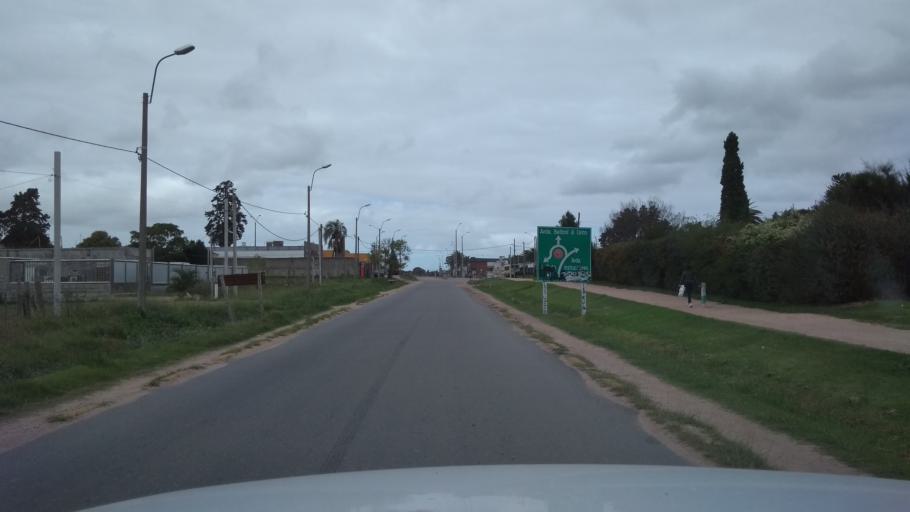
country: UY
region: Canelones
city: Toledo
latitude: -34.7793
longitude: -56.1369
